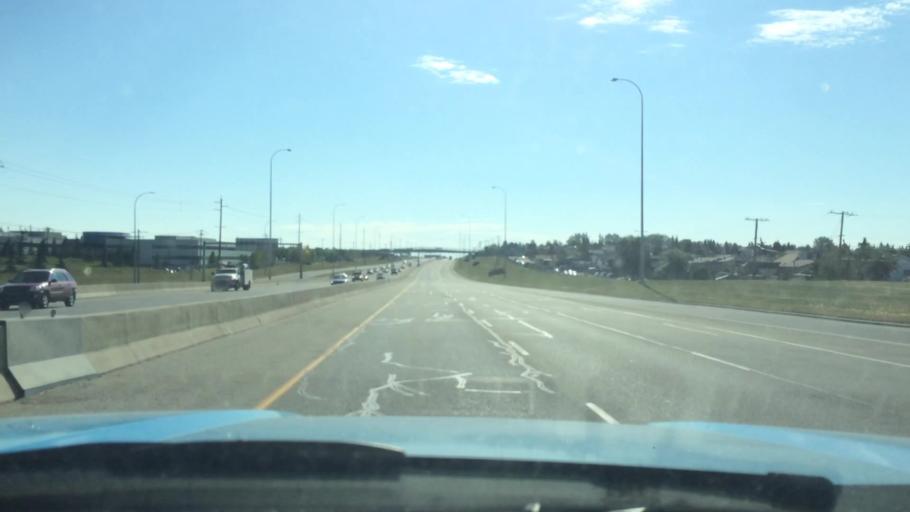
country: CA
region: Alberta
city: Calgary
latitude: 51.0959
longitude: -113.9796
